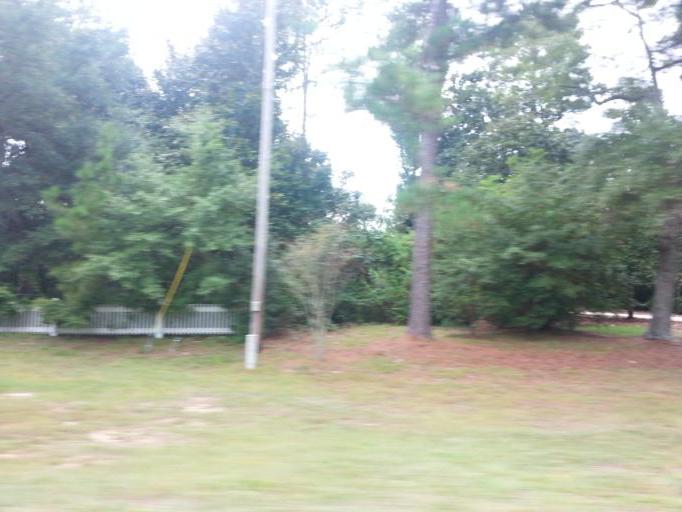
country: US
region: Alabama
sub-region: Baldwin County
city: Point Clear
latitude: 30.4592
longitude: -87.9164
